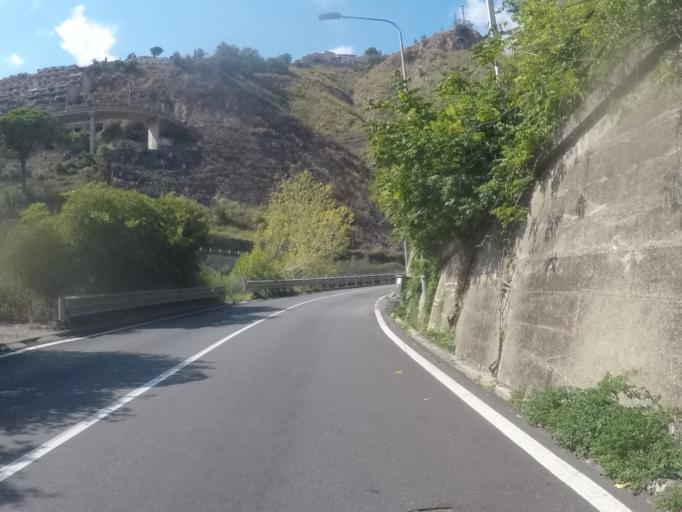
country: IT
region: Sicily
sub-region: Messina
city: Taormina
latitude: 37.8616
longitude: 15.2914
